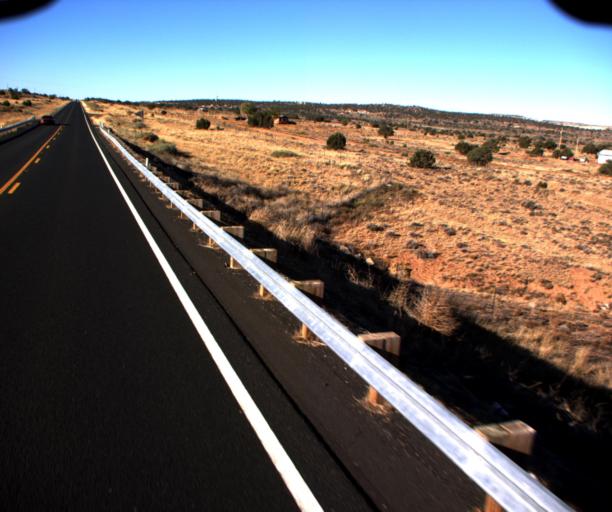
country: US
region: Arizona
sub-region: Apache County
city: Ganado
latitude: 35.7756
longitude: -109.7334
